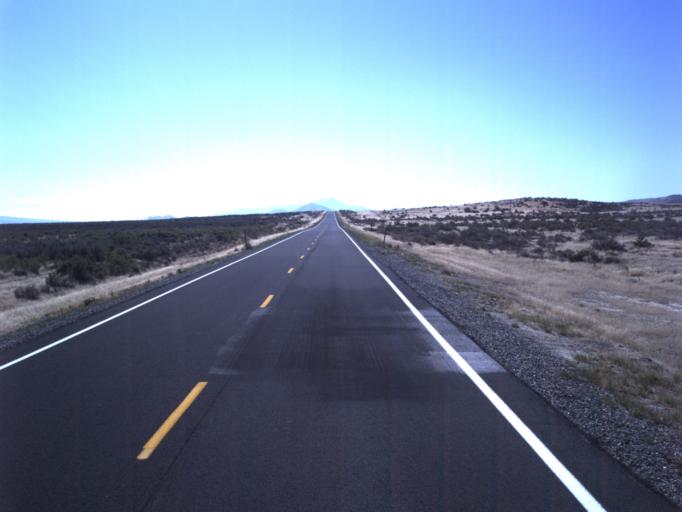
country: US
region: Utah
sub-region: Tooele County
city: Grantsville
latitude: 40.2970
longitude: -112.7426
